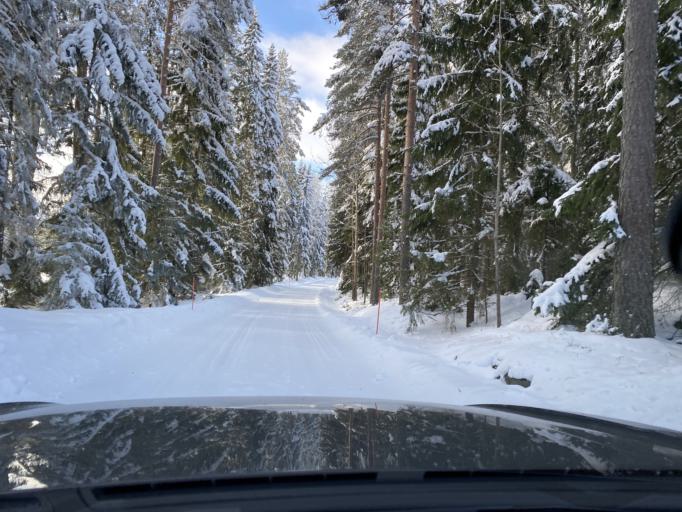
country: FI
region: Pirkanmaa
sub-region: Lounais-Pirkanmaa
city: Punkalaidun
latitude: 61.0695
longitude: 23.2538
